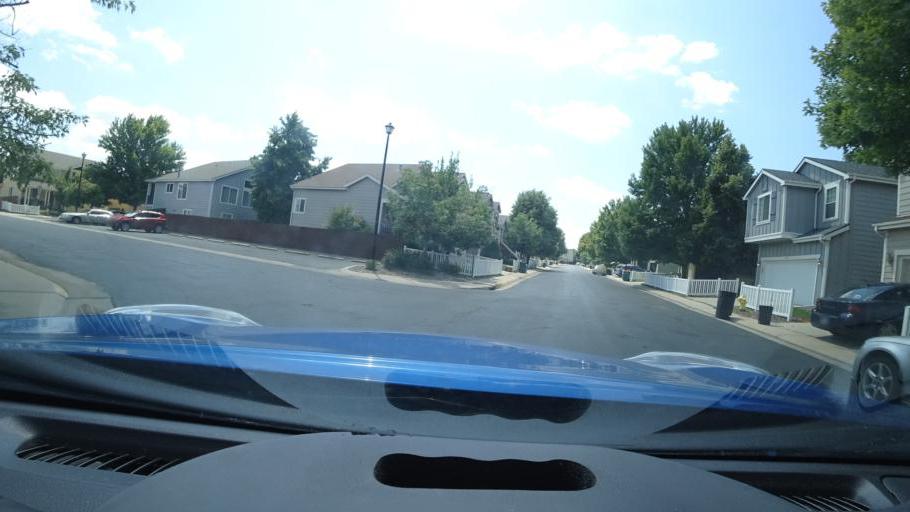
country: US
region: Colorado
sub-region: Arapahoe County
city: Glendale
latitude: 39.6941
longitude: -104.8819
